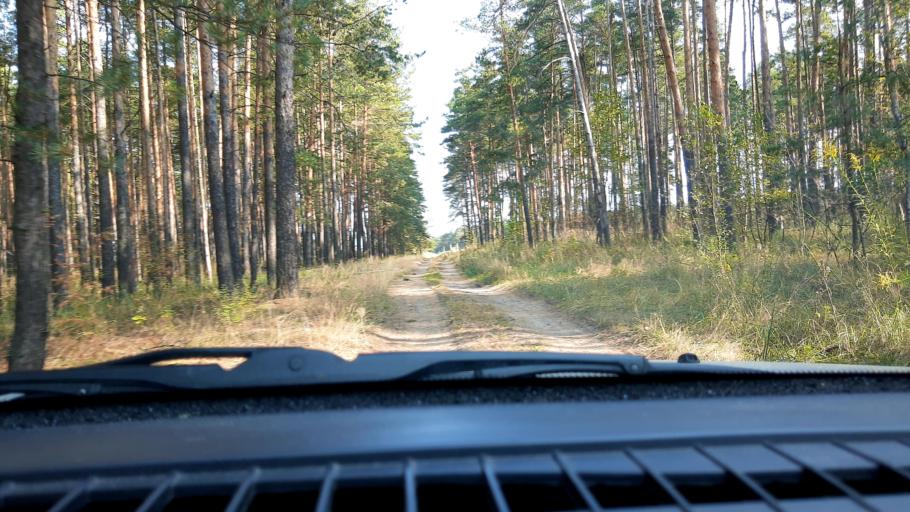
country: RU
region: Nizjnij Novgorod
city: Lukino
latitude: 56.4057
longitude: 43.6432
